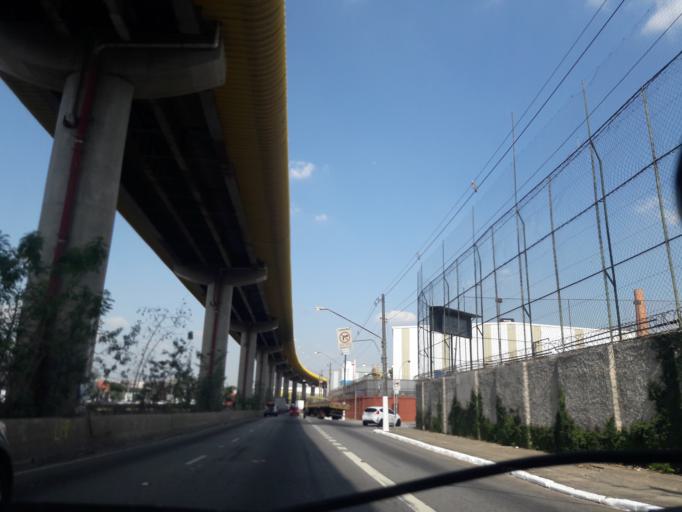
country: BR
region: Sao Paulo
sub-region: Sao Paulo
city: Sao Paulo
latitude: -23.5772
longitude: -46.6010
